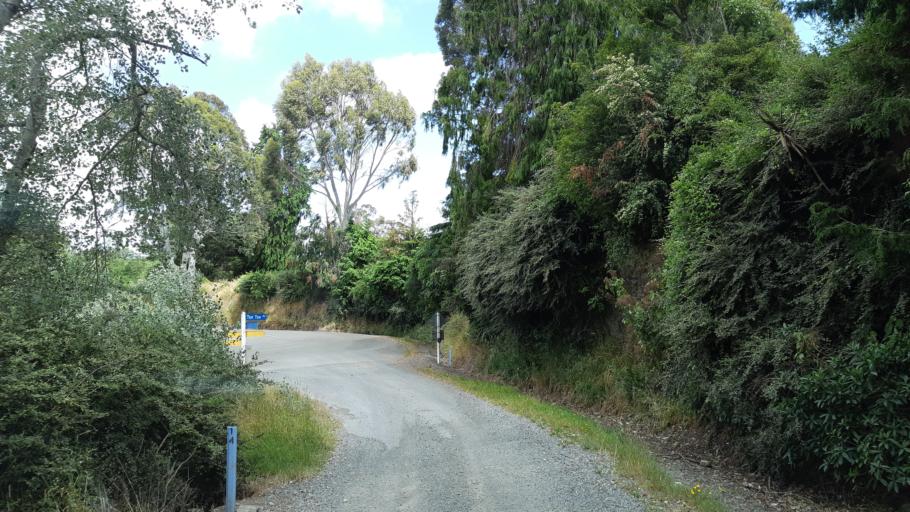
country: NZ
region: Manawatu-Wanganui
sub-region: Ruapehu District
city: Waiouru
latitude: -39.7832
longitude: 175.8968
